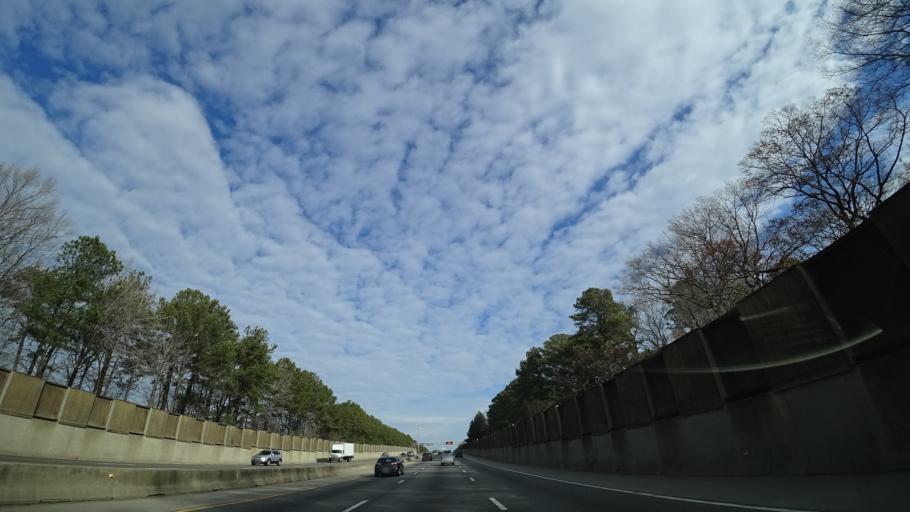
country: US
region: Virginia
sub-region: City of Hampton
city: Hampton
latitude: 37.0216
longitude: -76.3815
